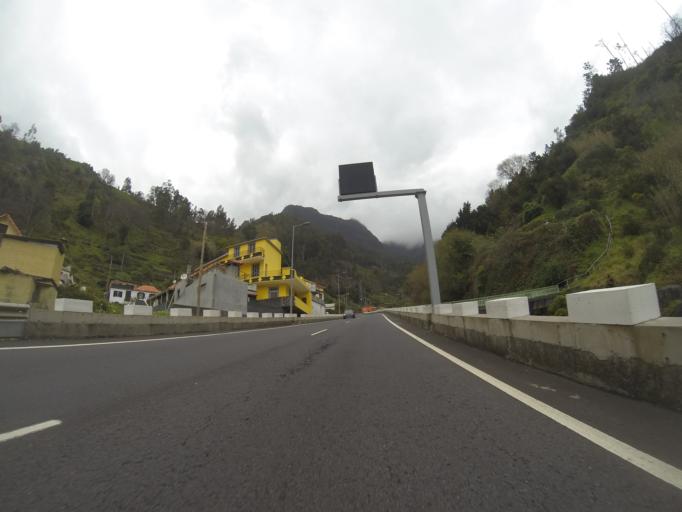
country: PT
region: Madeira
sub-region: Camara de Lobos
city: Curral das Freiras
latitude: 32.7393
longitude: -17.0191
